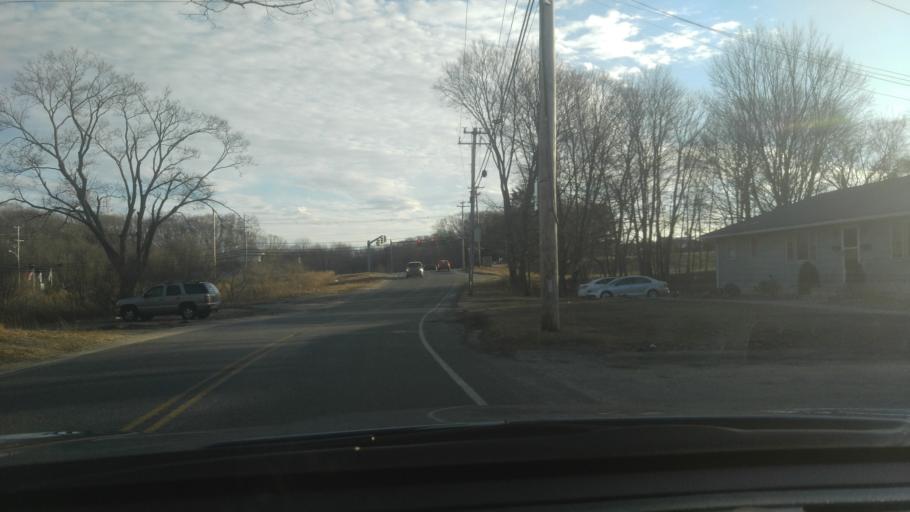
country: US
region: Rhode Island
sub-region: Washington County
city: Exeter
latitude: 41.5842
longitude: -71.4979
